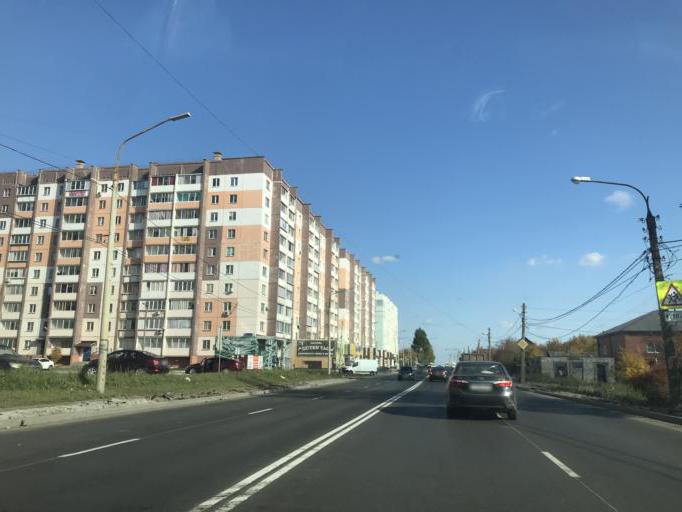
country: RU
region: Chelyabinsk
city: Roshchino
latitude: 55.2346
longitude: 61.3029
